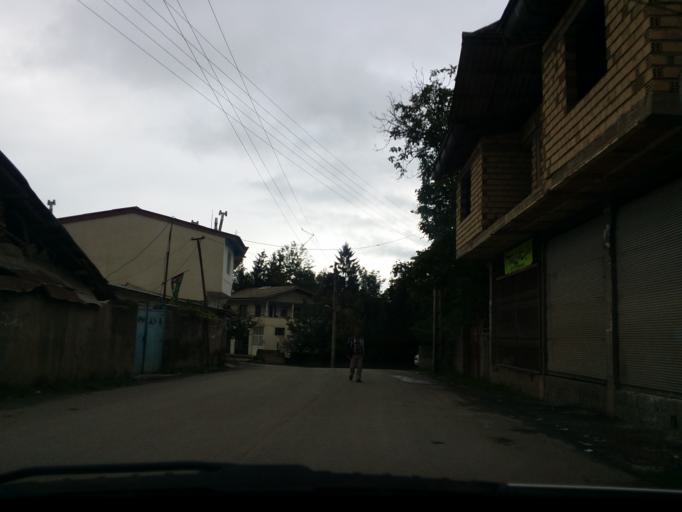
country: IR
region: Mazandaran
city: `Abbasabad
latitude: 36.5055
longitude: 51.1867
